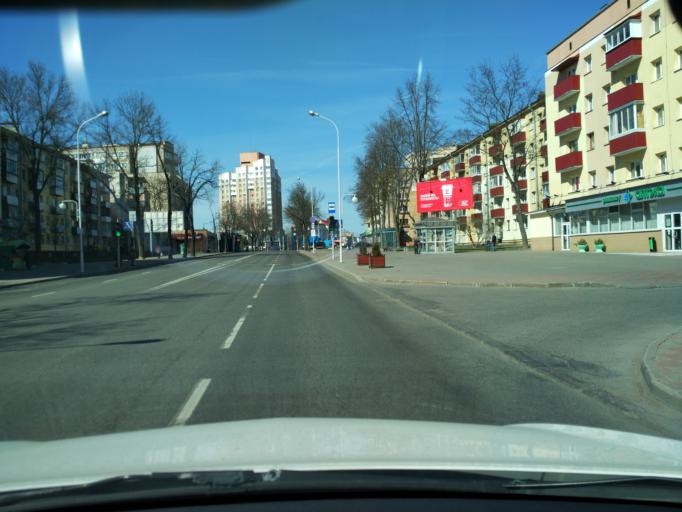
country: BY
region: Minsk
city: Minsk
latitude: 53.8760
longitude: 27.5348
